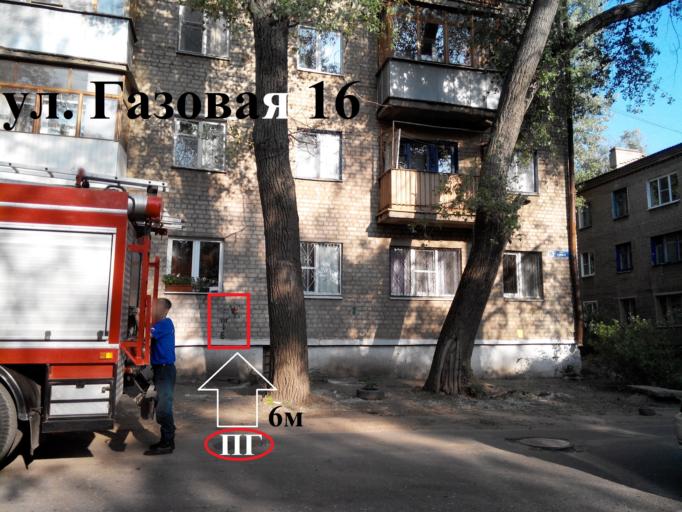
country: RU
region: Voronezj
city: Voronezh
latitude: 51.6761
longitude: 39.1396
